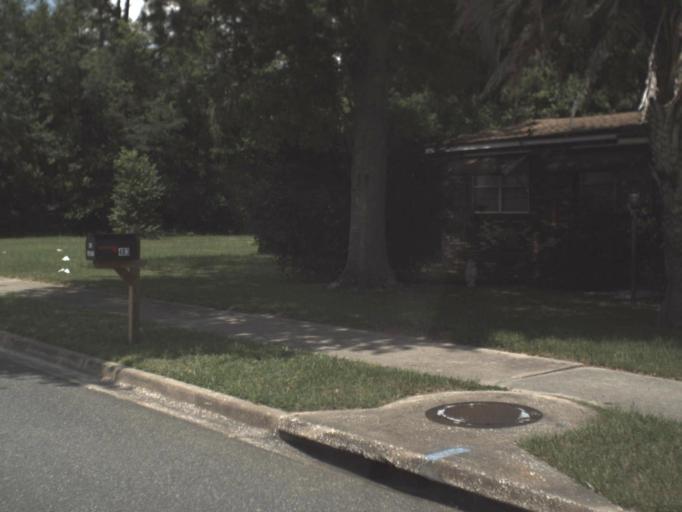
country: US
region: Florida
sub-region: Baker County
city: Macclenny
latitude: 30.2875
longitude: -82.1249
